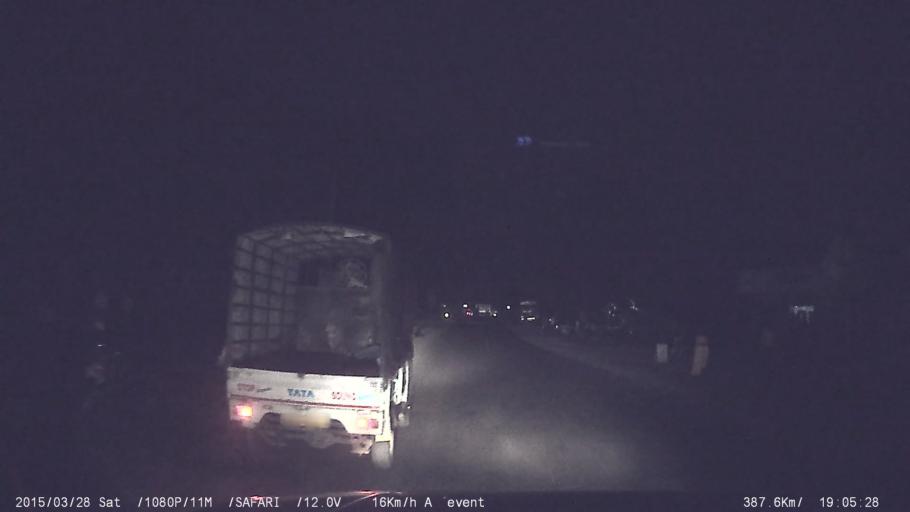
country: IN
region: Karnataka
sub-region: Mandya
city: Shrirangapattana
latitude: 12.3939
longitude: 76.6067
